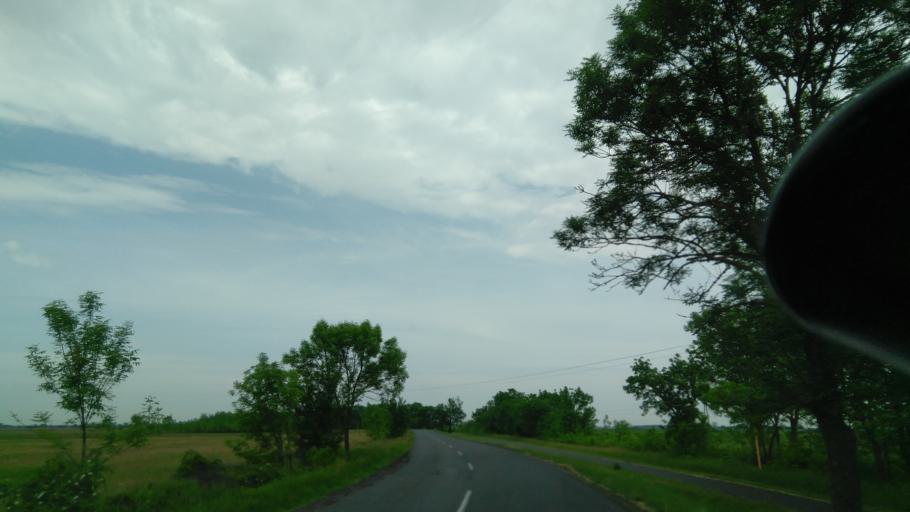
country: HU
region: Bekes
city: Szeghalom
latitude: 47.0564
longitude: 21.1955
